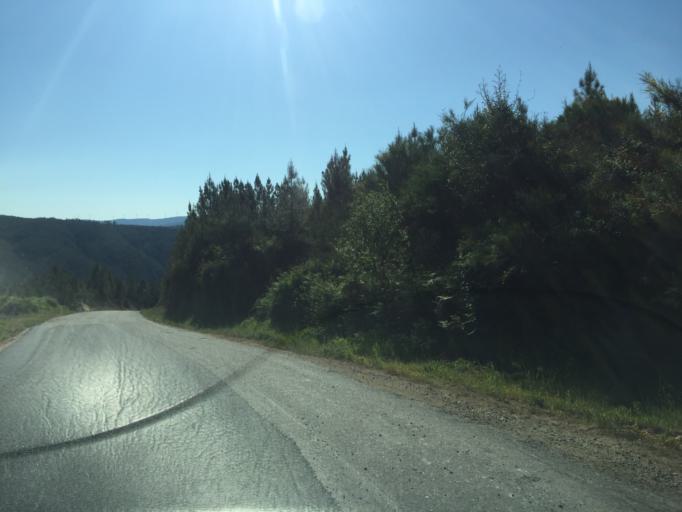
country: PT
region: Coimbra
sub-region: Pampilhosa da Serra
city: Pampilhosa da Serra
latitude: 40.0498
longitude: -7.8185
